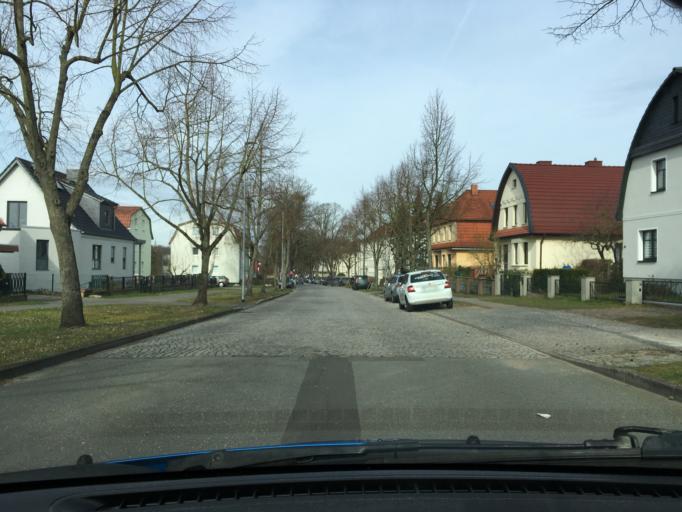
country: DE
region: Mecklenburg-Vorpommern
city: Feldstadt
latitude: 53.6060
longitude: 11.4185
